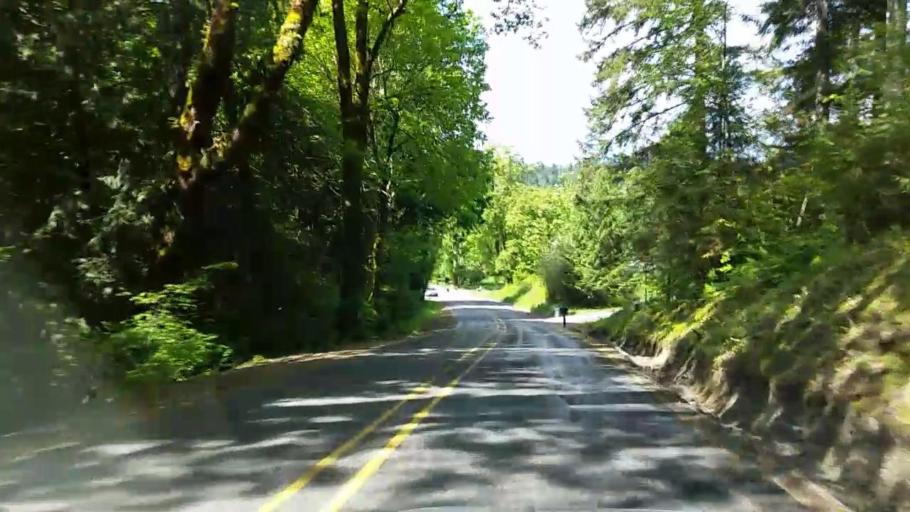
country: US
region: Washington
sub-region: Pierce County
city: Key Center
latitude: 47.3393
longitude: -122.7596
